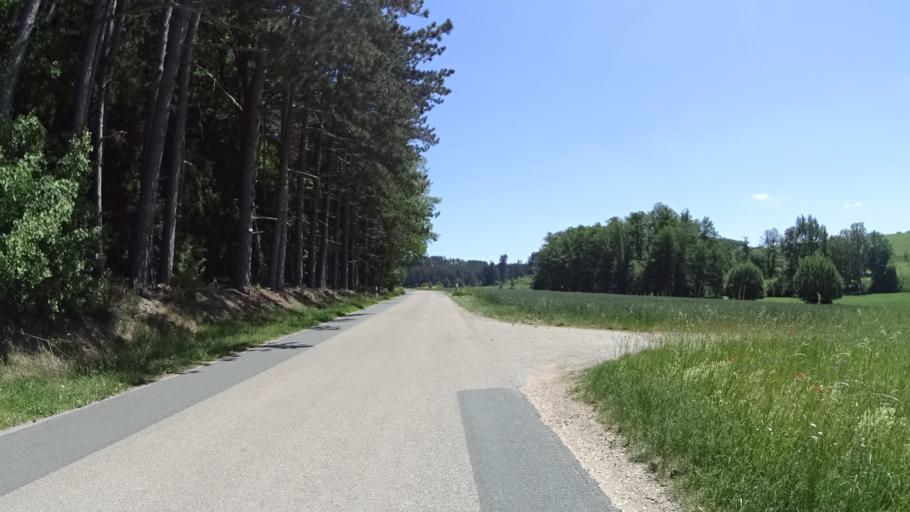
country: DE
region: Bavaria
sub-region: Regierungsbezirk Mittelfranken
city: Pleinfeld
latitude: 49.0831
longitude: 10.9794
